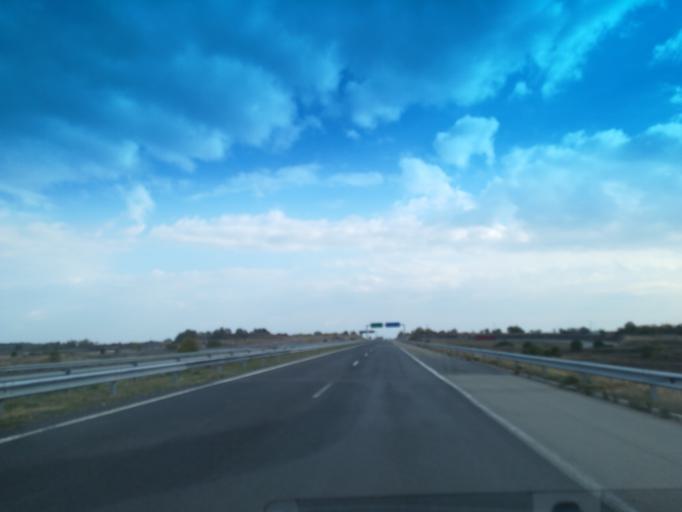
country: BG
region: Stara Zagora
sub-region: Obshtina Chirpan
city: Chirpan
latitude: 42.2494
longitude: 25.4090
